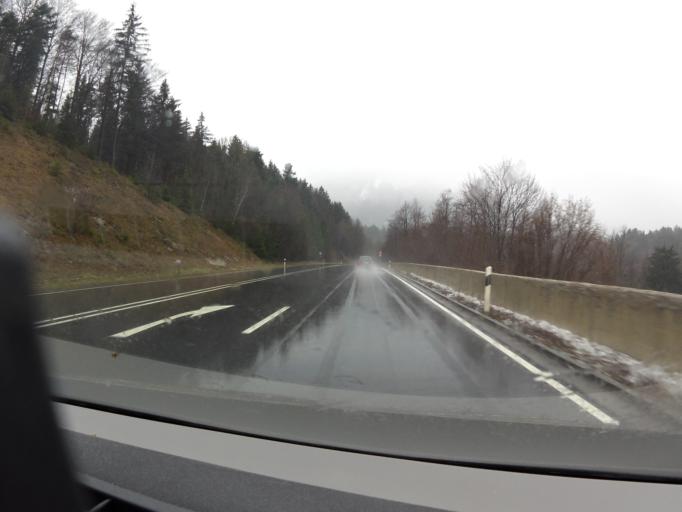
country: DE
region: Bavaria
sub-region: Upper Bavaria
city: Bad Toelz
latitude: 47.7541
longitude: 11.5398
